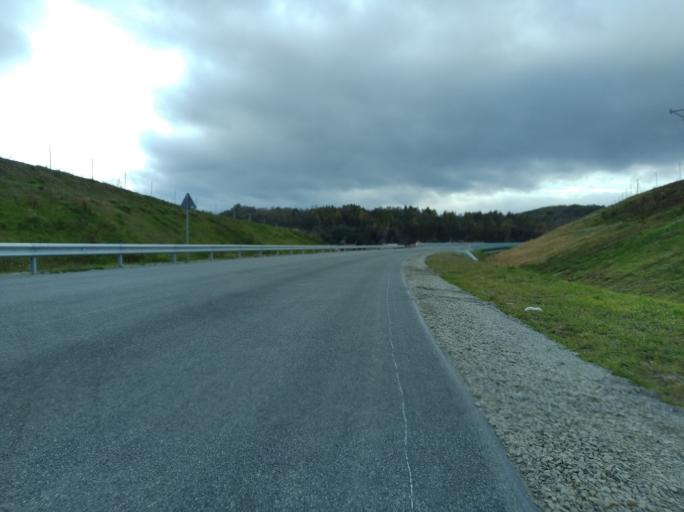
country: PL
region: Subcarpathian Voivodeship
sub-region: Powiat strzyzowski
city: Strzyzow
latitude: 49.8647
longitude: 21.8194
